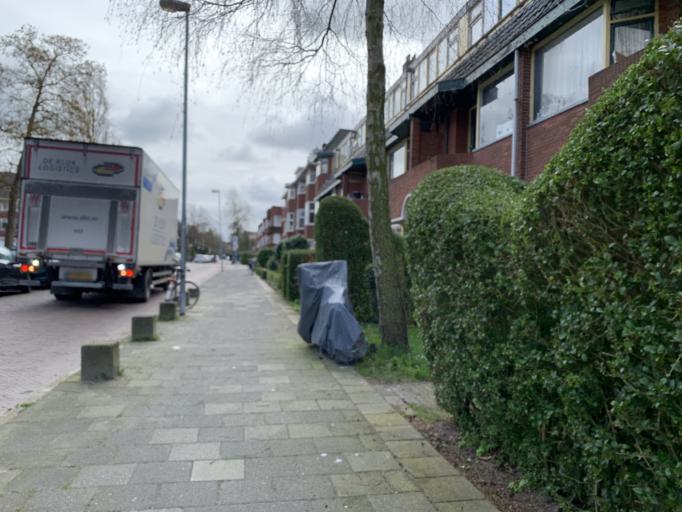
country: NL
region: Groningen
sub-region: Gemeente Groningen
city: Korrewegwijk
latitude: 53.2335
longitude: 6.5738
